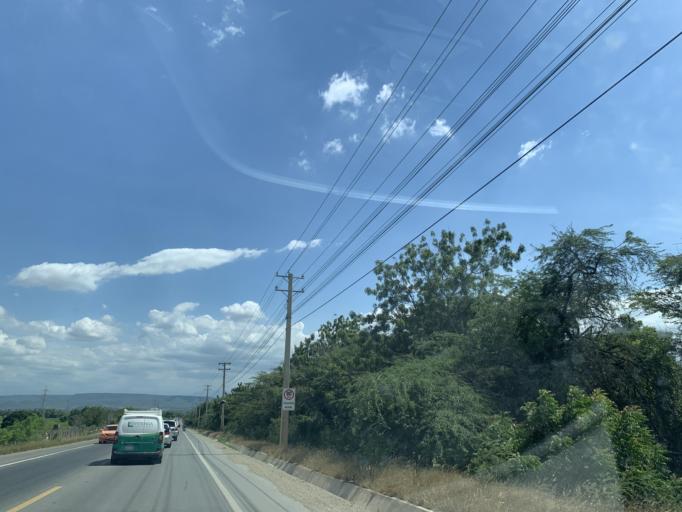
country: DO
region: Santiago
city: Villa Bisono
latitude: 19.5679
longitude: -70.8566
